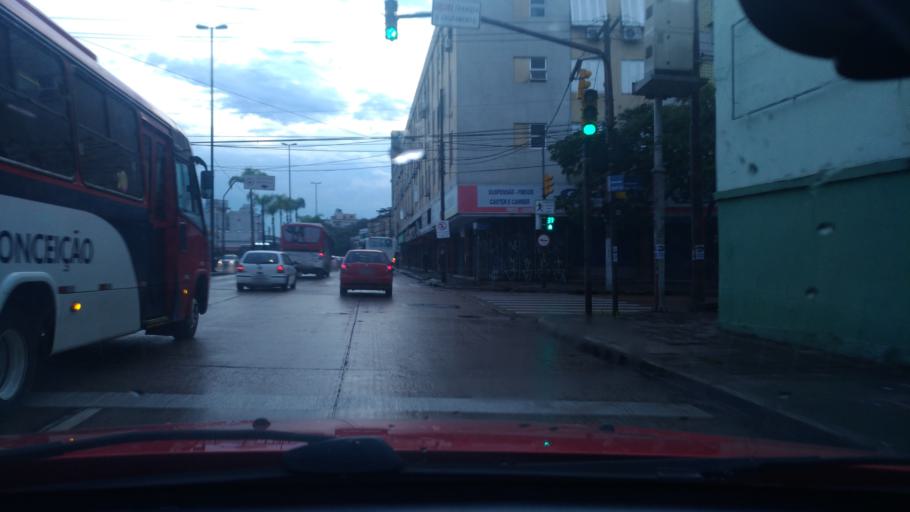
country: BR
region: Rio Grande do Sul
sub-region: Porto Alegre
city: Porto Alegre
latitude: -30.0224
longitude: -51.2124
